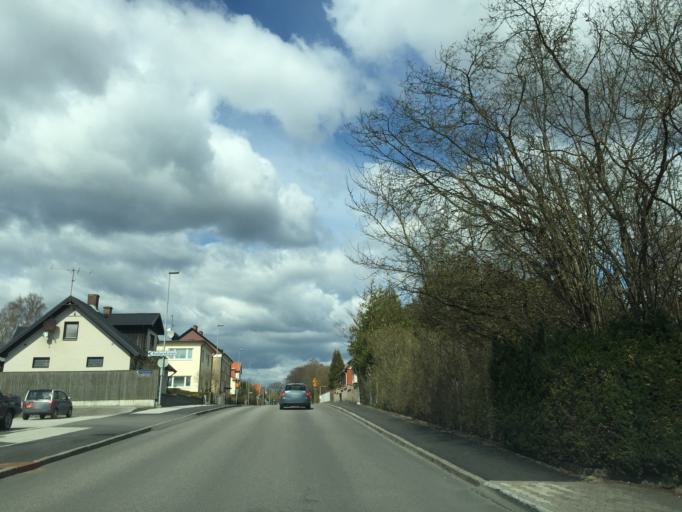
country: SE
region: Skane
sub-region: Horby Kommun
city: Hoerby
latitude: 55.8513
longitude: 13.6554
